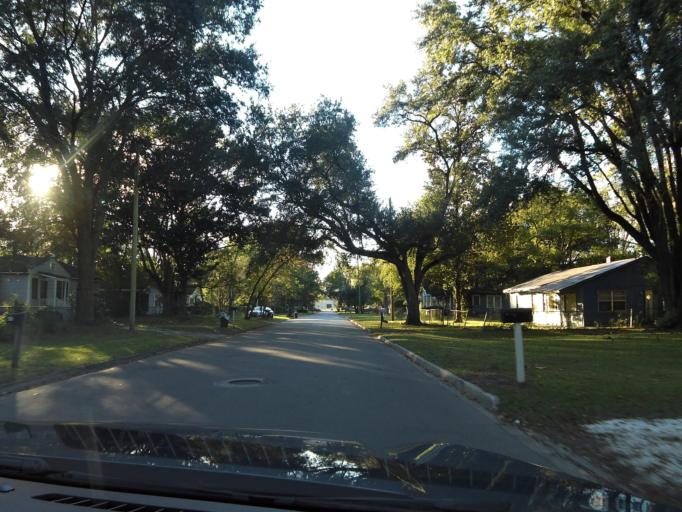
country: US
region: Florida
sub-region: Duval County
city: Jacksonville
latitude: 30.3534
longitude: -81.7197
